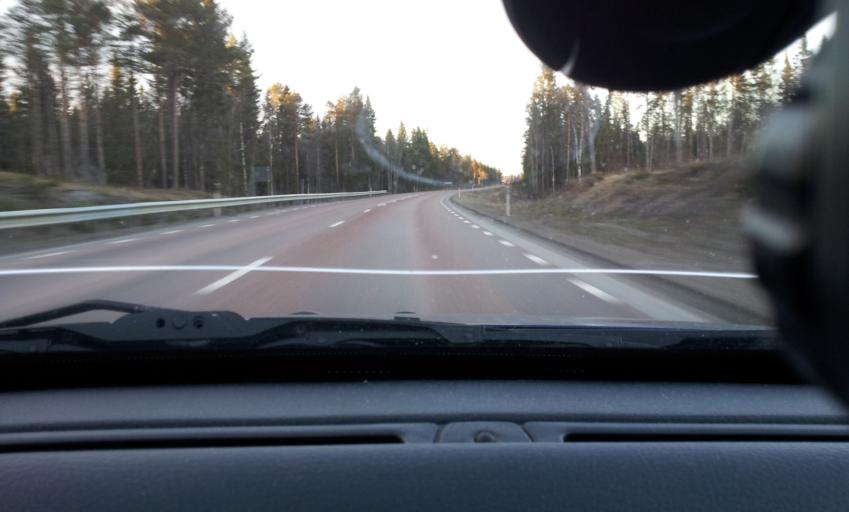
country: SE
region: Jaemtland
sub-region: Bergs Kommun
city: Hoverberg
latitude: 62.9504
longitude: 14.5450
